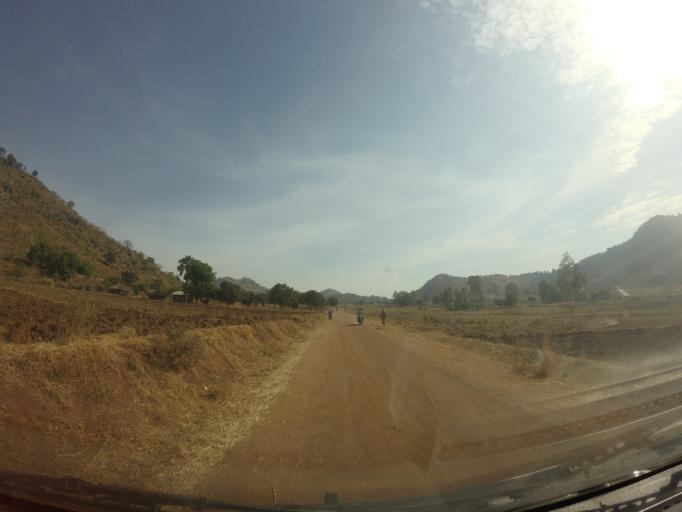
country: UG
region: Northern Region
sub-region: Maracha District
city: Maracha
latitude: 3.2104
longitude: 31.0380
